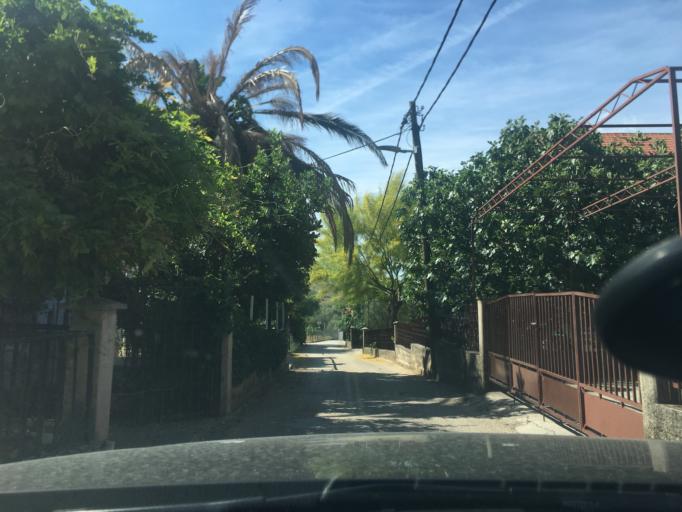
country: HR
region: Splitsko-Dalmatinska
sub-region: Grad Trogir
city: Trogir
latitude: 43.5246
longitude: 16.2611
